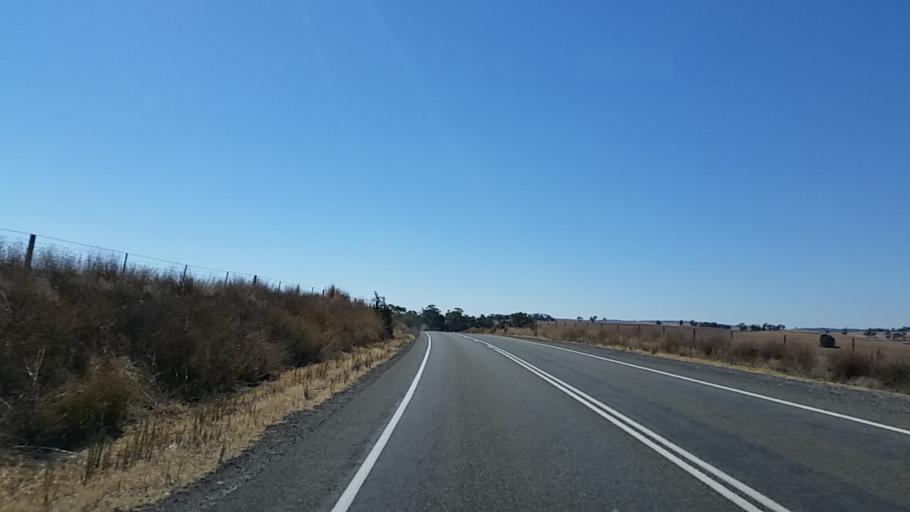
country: AU
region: South Australia
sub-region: Clare and Gilbert Valleys
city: Clare
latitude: -34.0662
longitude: 138.7915
